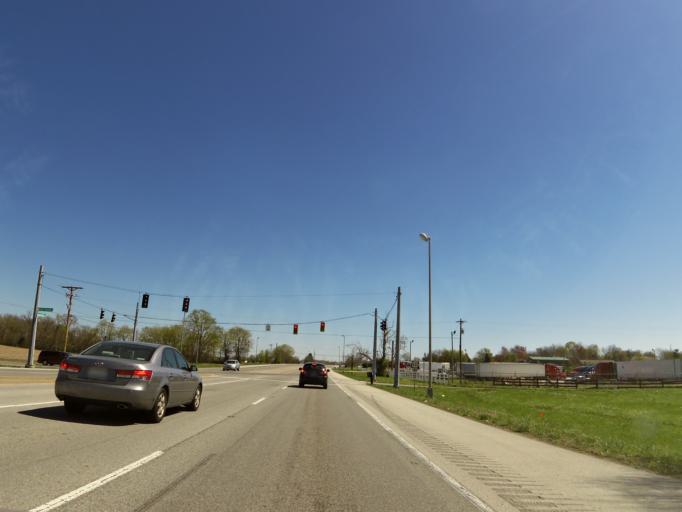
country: US
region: Kentucky
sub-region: Warren County
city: Bowling Green
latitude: 36.9530
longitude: -86.5088
